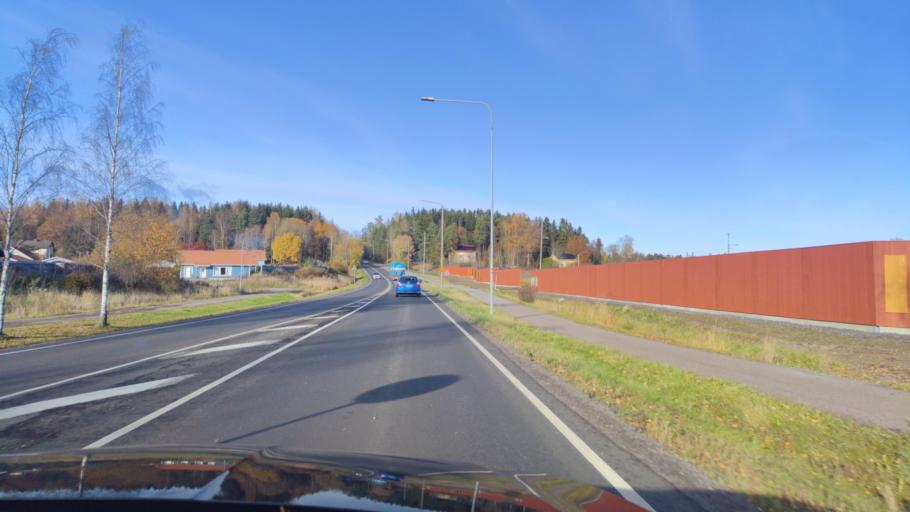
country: FI
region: Varsinais-Suomi
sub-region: Turku
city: Kaarina
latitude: 60.4374
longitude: 22.3840
